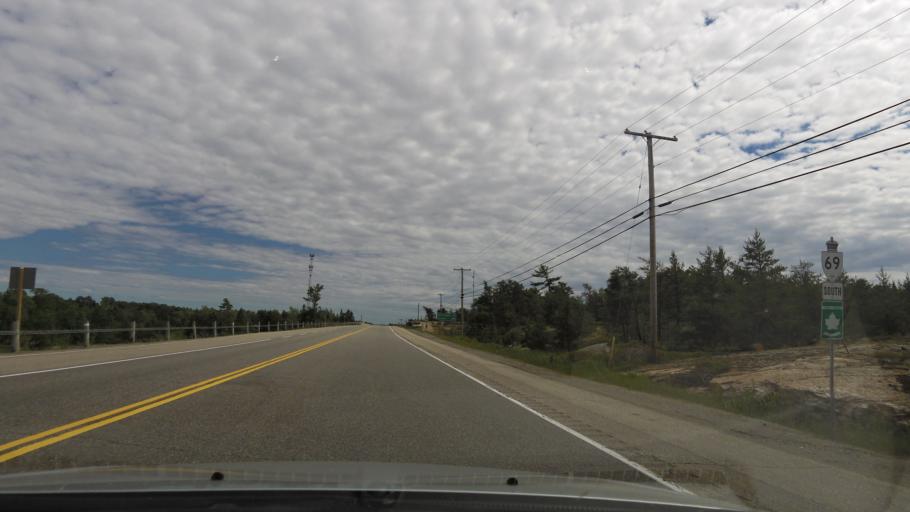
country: CA
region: Ontario
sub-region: Parry Sound District
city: Parry Sound
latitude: 45.8028
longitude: -80.5375
